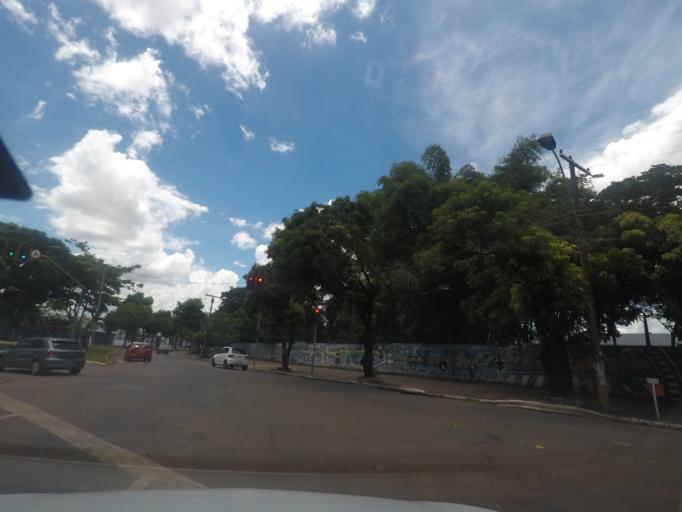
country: BR
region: Goias
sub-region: Goiania
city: Goiania
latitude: -16.6817
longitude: -49.3103
